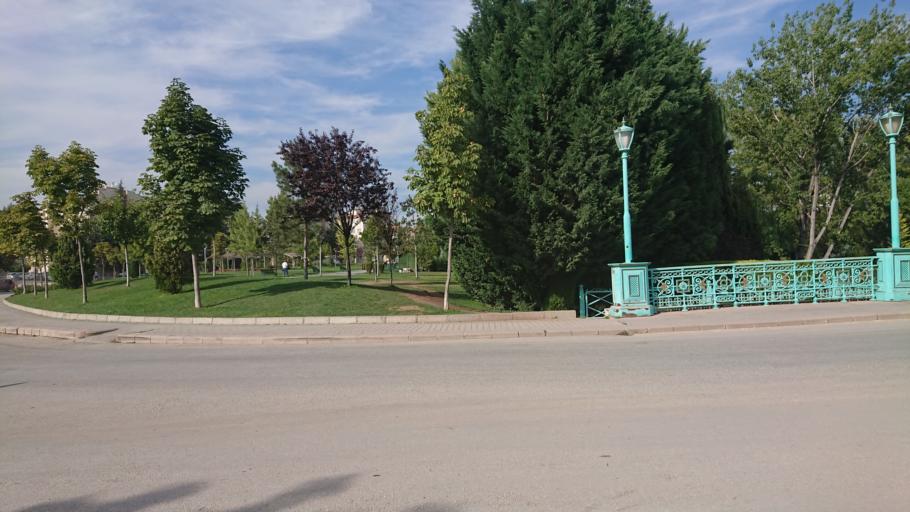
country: TR
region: Eskisehir
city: Eskisehir
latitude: 39.7704
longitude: 30.4985
